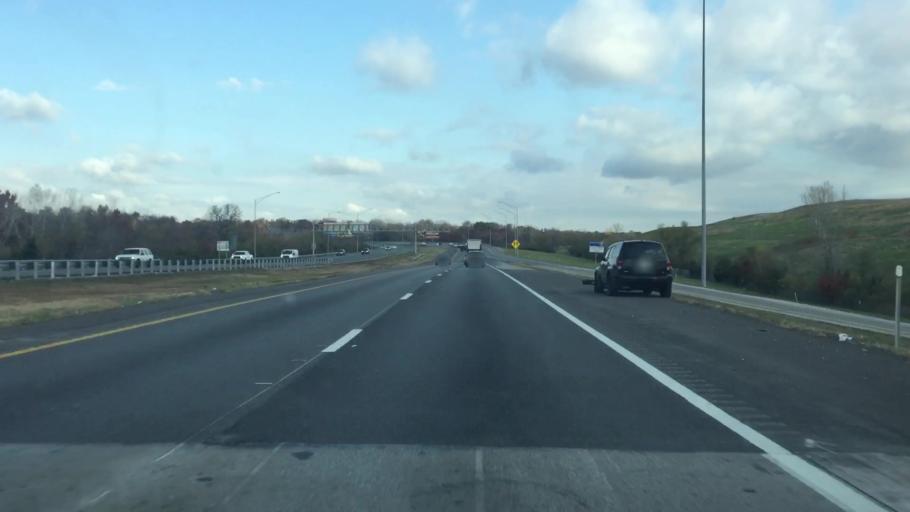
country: US
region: Kansas
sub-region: Johnson County
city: Leawood
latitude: 38.9744
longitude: -94.5458
